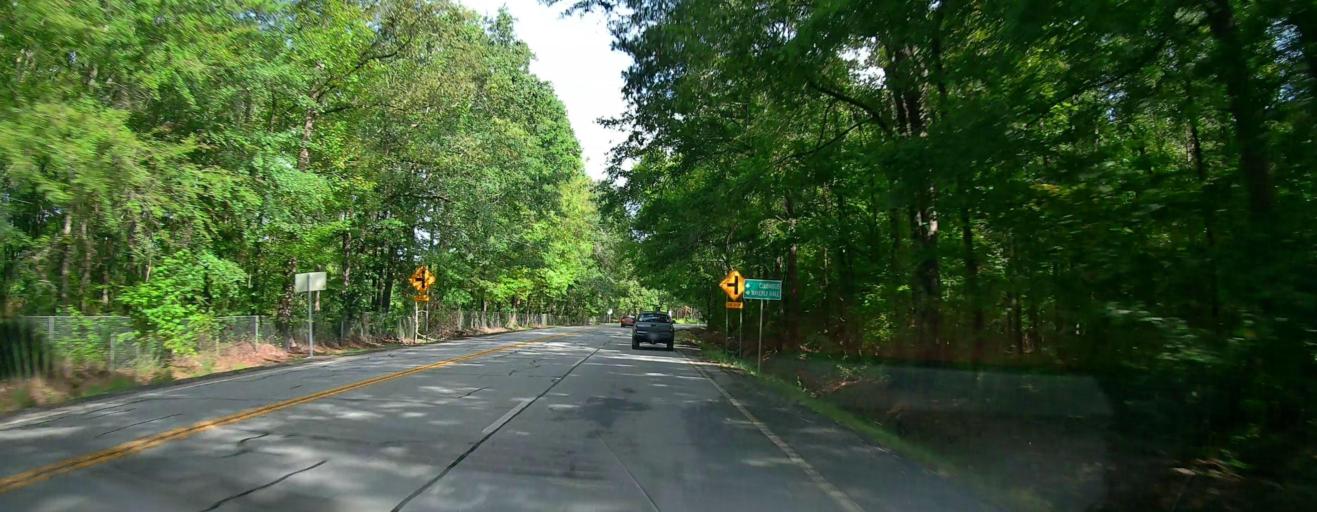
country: US
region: Georgia
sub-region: Harris County
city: Hamilton
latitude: 32.7032
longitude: -84.8617
